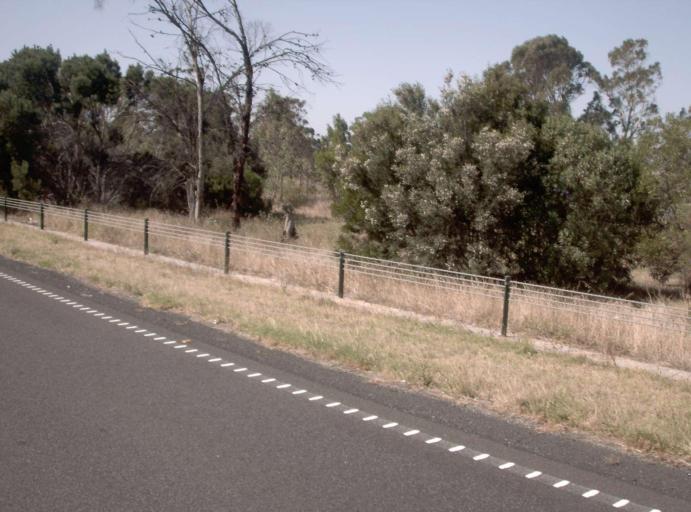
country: AU
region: Victoria
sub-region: Kingston
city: Chelsea Heights
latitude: -38.0367
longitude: 145.1388
